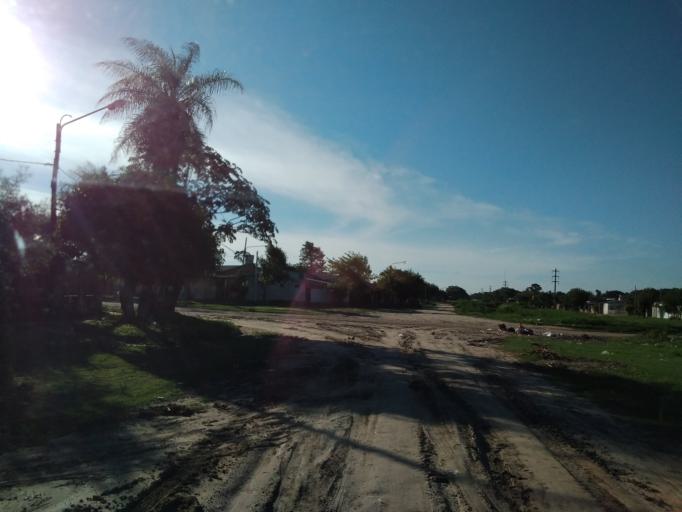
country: AR
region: Corrientes
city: Corrientes
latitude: -27.5068
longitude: -58.7781
